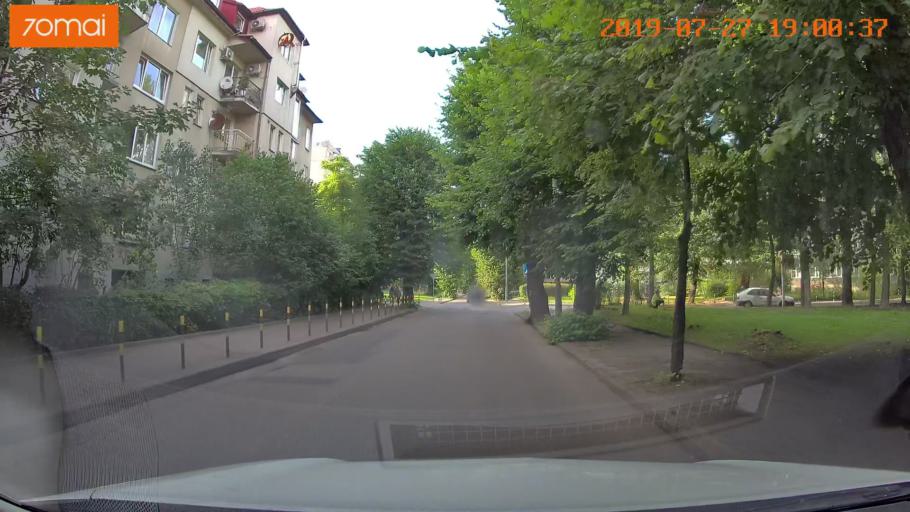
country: RU
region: Kaliningrad
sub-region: Gorod Kaliningrad
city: Kaliningrad
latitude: 54.7273
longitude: 20.4846
